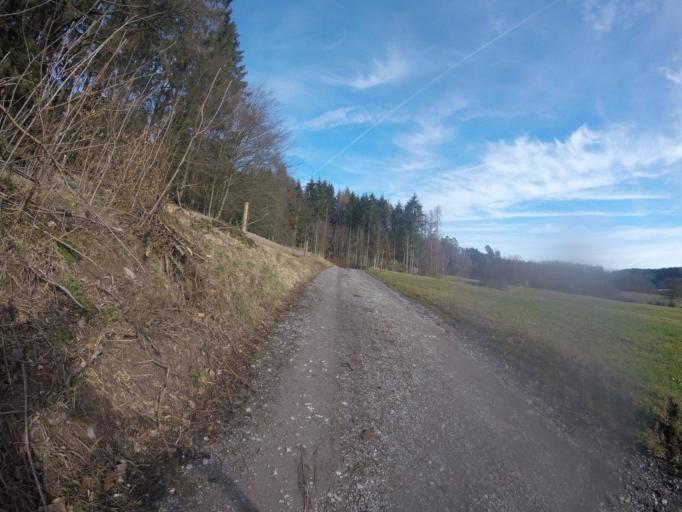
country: DE
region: Baden-Wuerttemberg
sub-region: Regierungsbezirk Stuttgart
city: Oberrot
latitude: 48.9874
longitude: 9.6560
